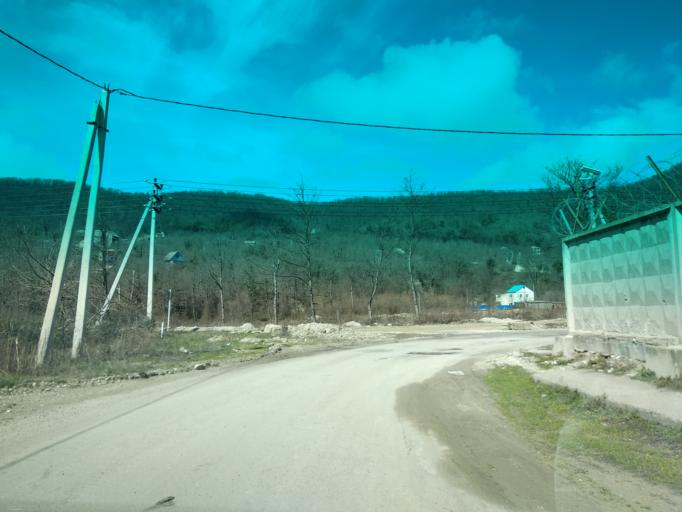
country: RU
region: Krasnodarskiy
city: Shepsi
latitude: 44.0532
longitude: 39.1625
